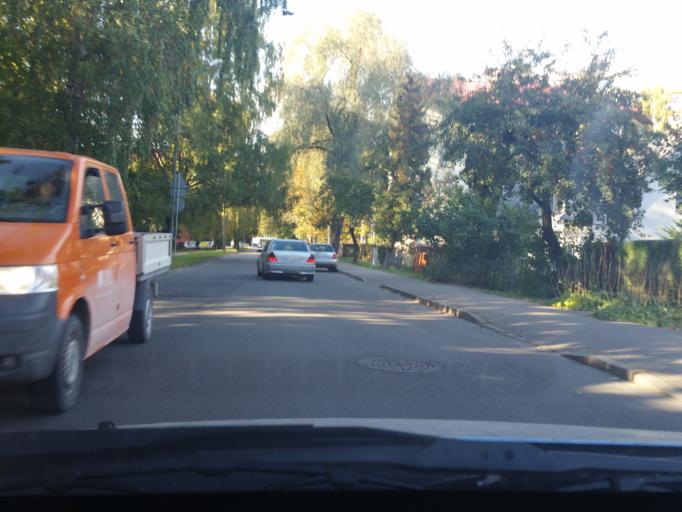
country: LV
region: Riga
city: Jaunciems
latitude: 56.9637
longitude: 24.1797
